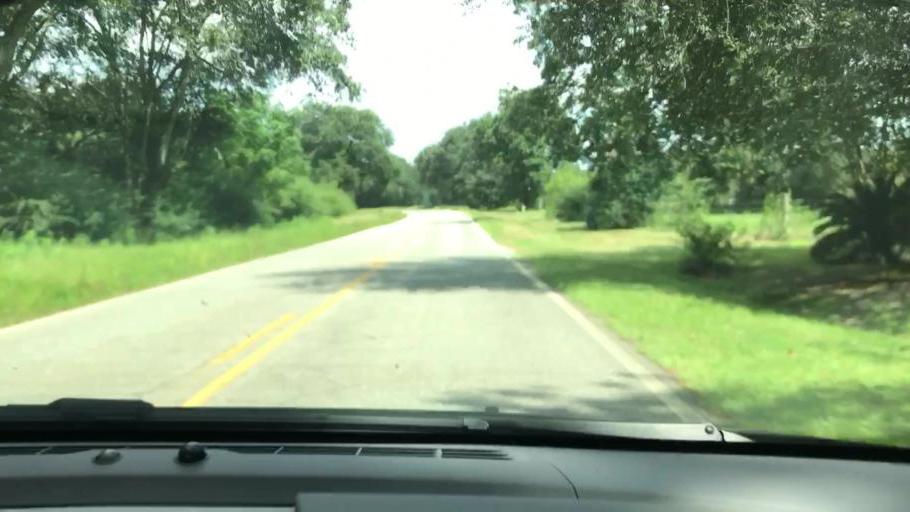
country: US
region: Georgia
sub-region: Early County
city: Blakely
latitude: 31.2225
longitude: -85.0027
